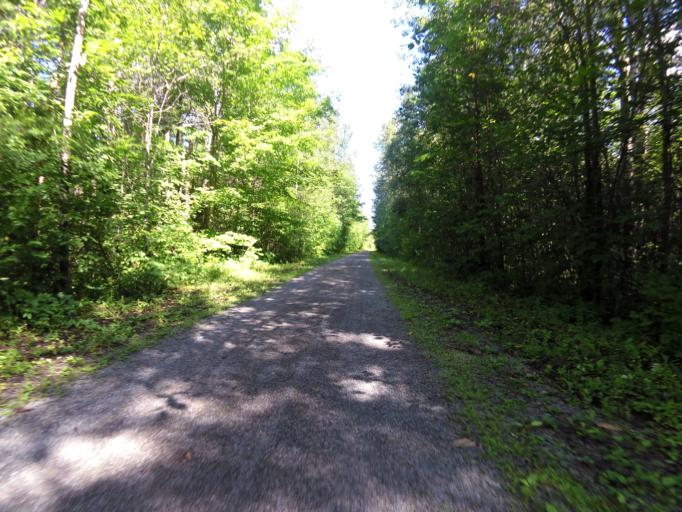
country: CA
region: Ontario
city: Ottawa
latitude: 45.2084
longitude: -75.6251
